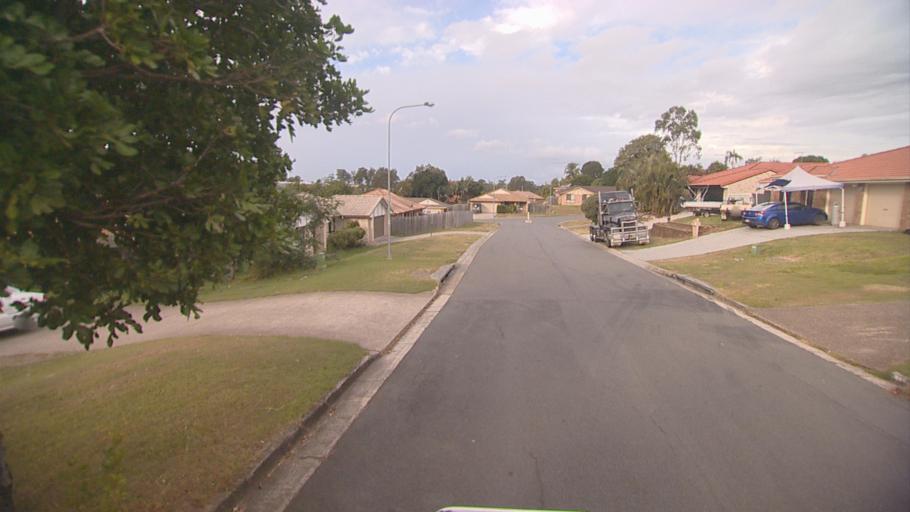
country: AU
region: Queensland
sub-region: Logan
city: Park Ridge South
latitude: -27.6804
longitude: 153.0239
